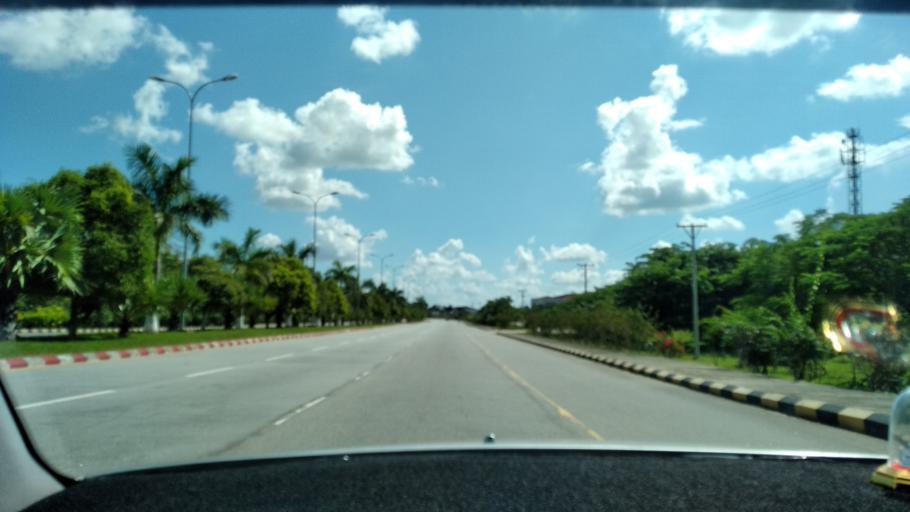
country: MM
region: Mandalay
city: Nay Pyi Taw
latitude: 19.7819
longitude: 96.1441
